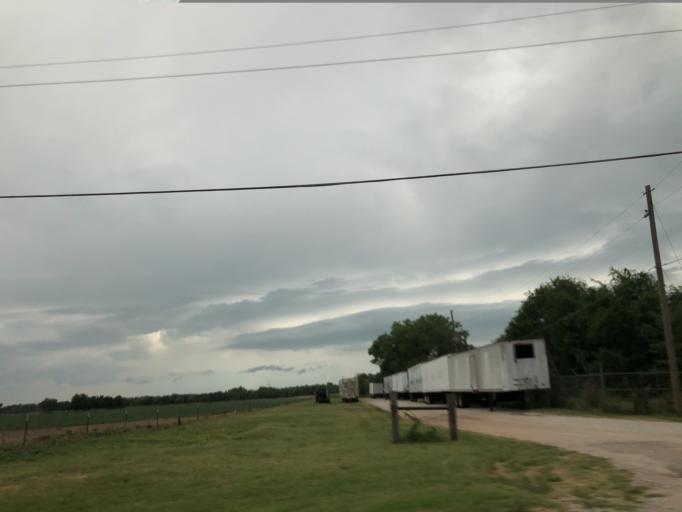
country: US
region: Kansas
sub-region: Reno County
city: Hutchinson
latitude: 38.1148
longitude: -97.9504
